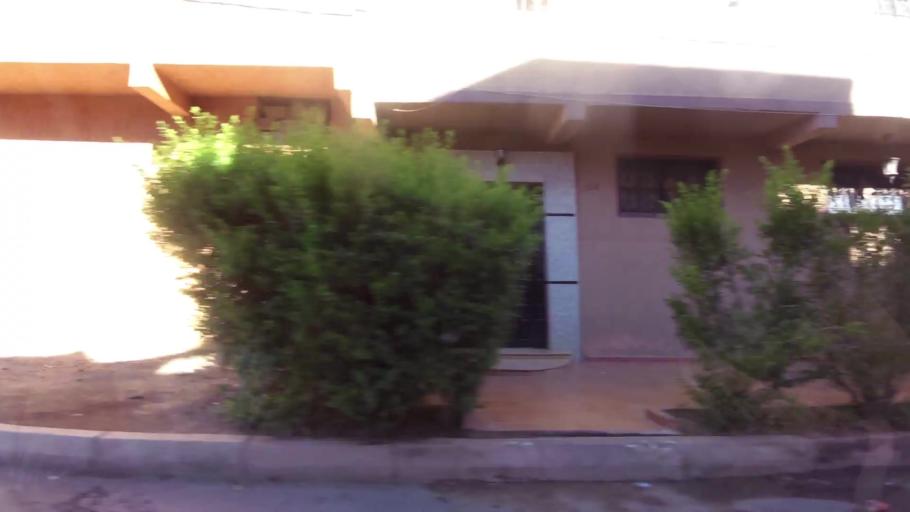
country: MA
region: Marrakech-Tensift-Al Haouz
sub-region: Marrakech
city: Marrakesh
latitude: 31.5998
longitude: -8.0364
